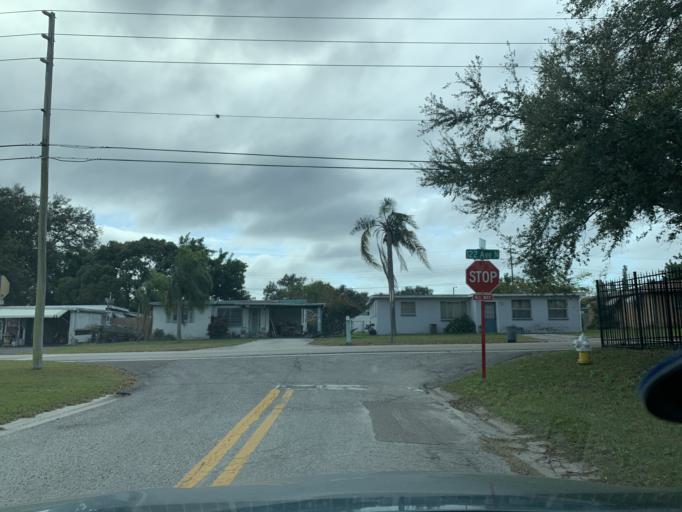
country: US
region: Florida
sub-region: Pinellas County
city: Ridgecrest
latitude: 27.8839
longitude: -82.7854
